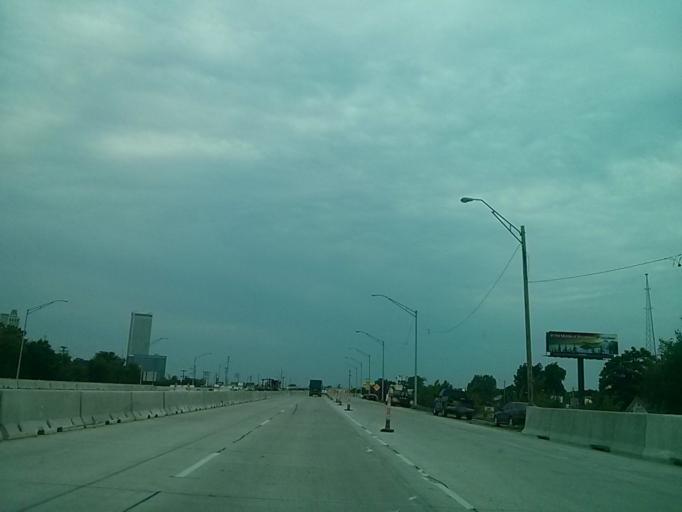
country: US
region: Oklahoma
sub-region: Tulsa County
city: Tulsa
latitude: 36.1594
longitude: -95.9716
